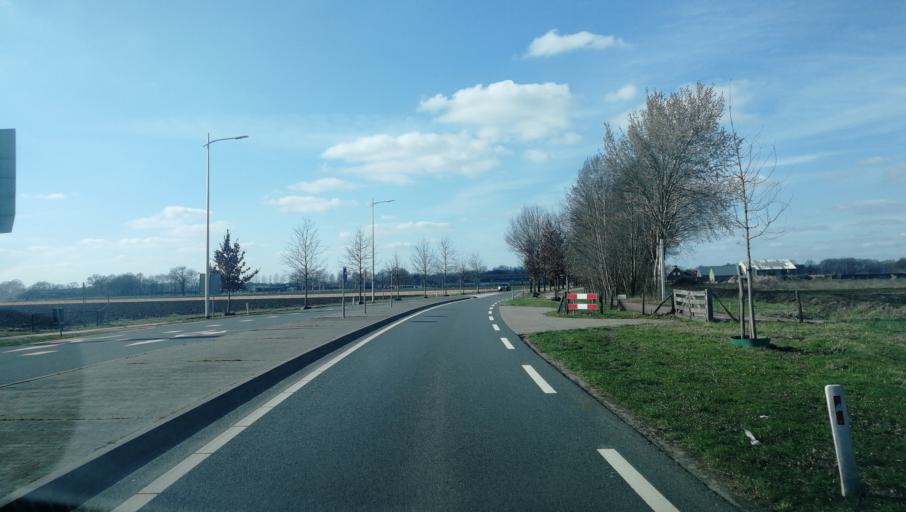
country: NL
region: Limburg
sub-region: Gemeente Peel en Maas
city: Maasbree
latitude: 51.4024
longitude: 6.0668
